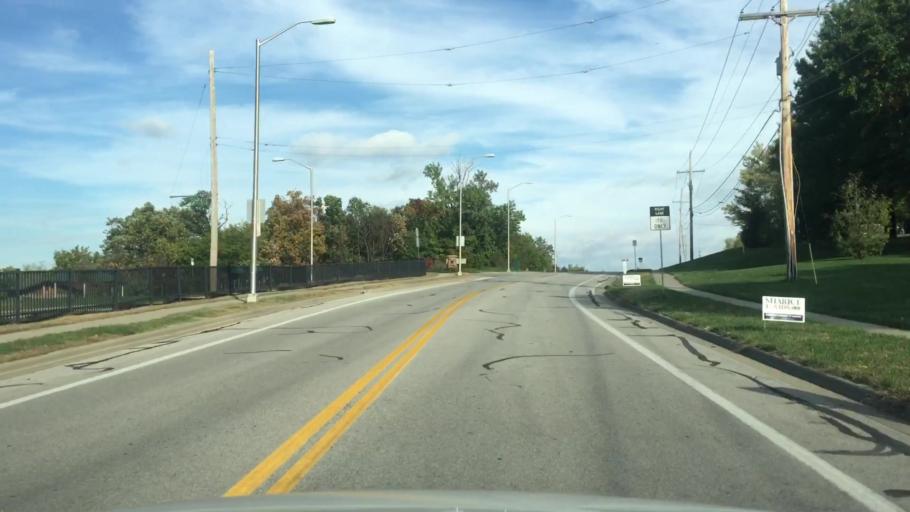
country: US
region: Kansas
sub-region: Johnson County
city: Shawnee
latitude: 39.0366
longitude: -94.7450
